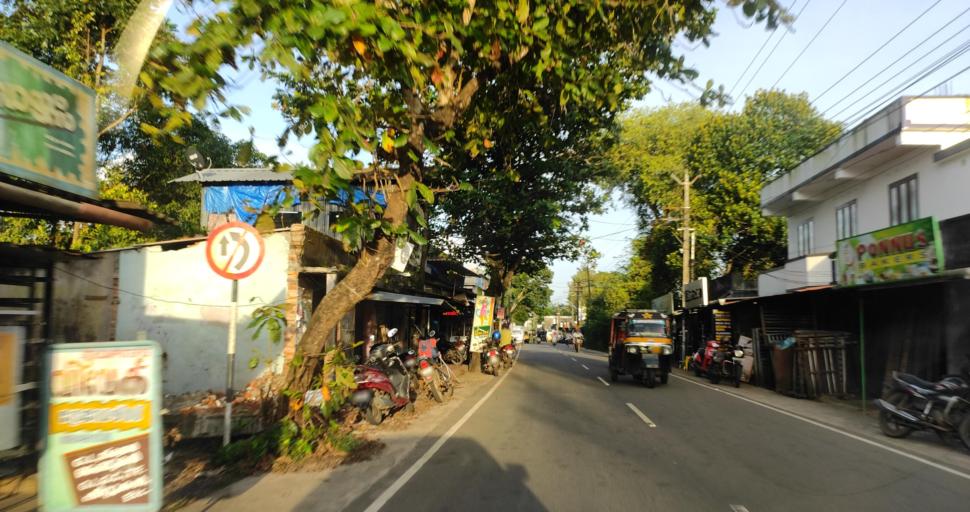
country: IN
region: Kerala
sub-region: Alappuzha
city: Shertallai
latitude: 9.6065
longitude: 76.3571
